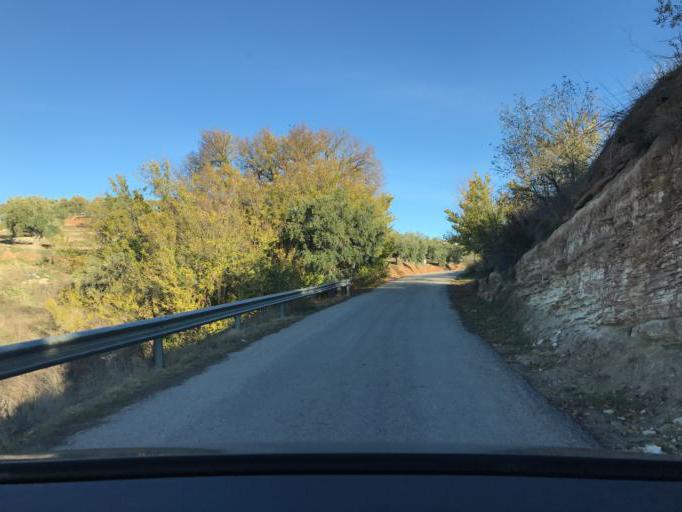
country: ES
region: Andalusia
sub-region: Provincia de Granada
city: Calicasas
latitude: 37.2739
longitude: -3.6228
